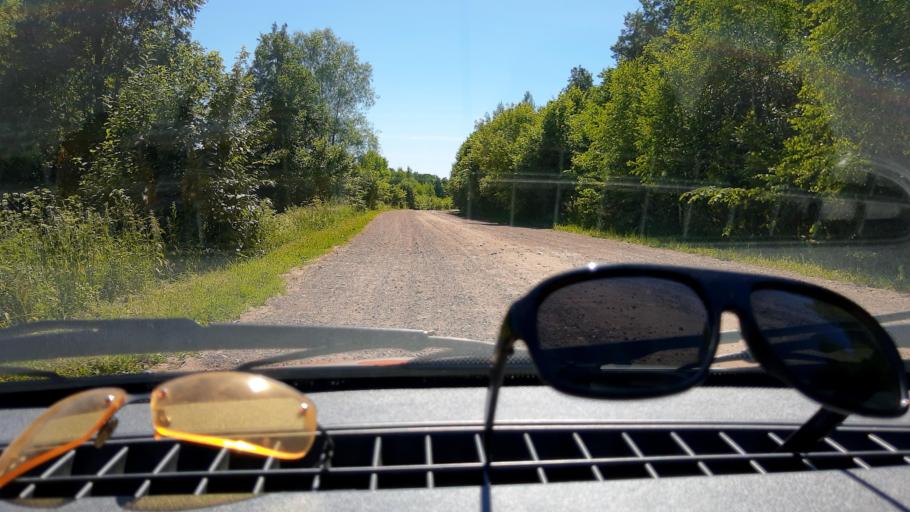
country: RU
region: Bashkortostan
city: Ulu-Telyak
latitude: 54.7863
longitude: 56.9968
